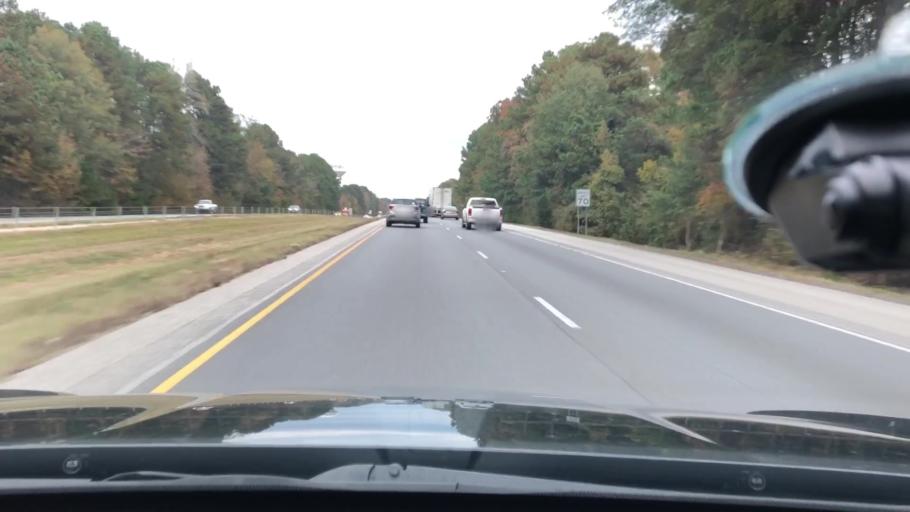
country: US
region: Arkansas
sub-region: Clark County
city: Arkadelphia
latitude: 34.1275
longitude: -93.0880
